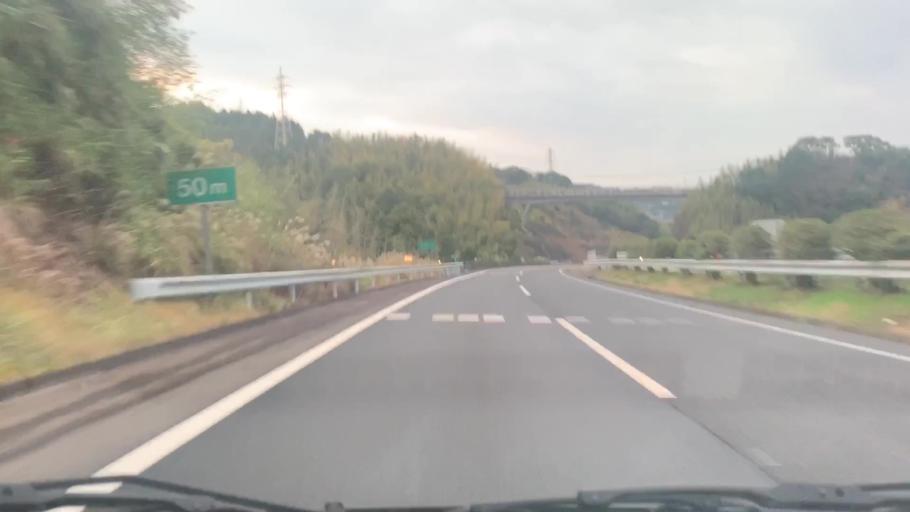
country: JP
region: Nagasaki
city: Omura
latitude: 33.0085
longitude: 129.9535
